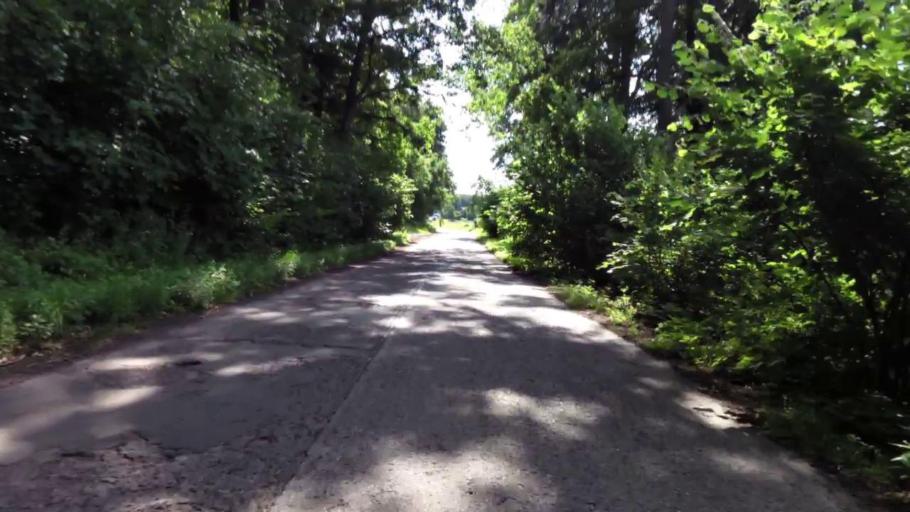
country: PL
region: West Pomeranian Voivodeship
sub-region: Powiat stargardzki
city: Dobrzany
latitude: 53.3903
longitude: 15.4873
